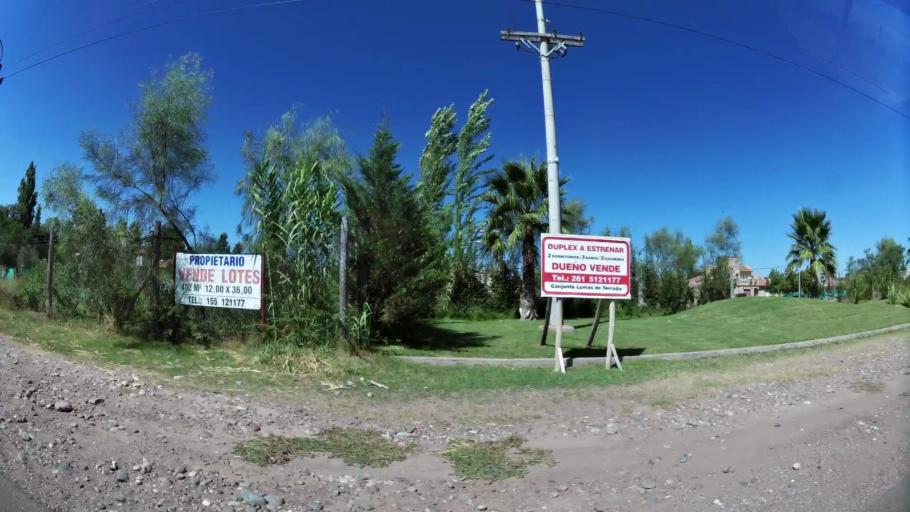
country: AR
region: Mendoza
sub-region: Departamento de Godoy Cruz
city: Godoy Cruz
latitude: -32.9811
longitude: -68.8427
